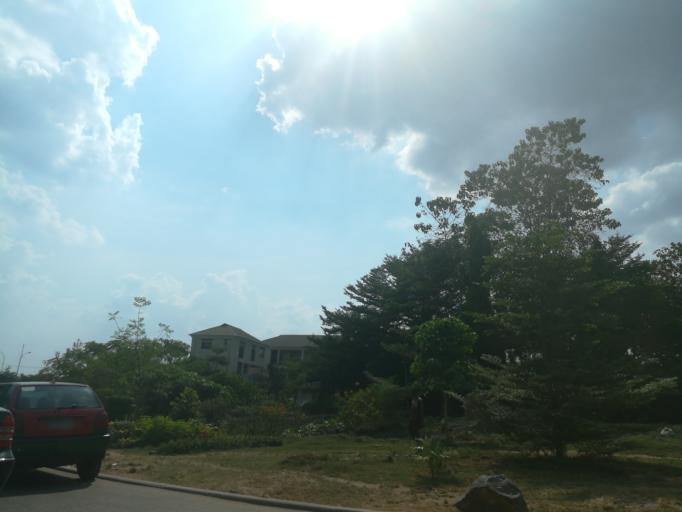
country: NG
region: Abuja Federal Capital Territory
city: Abuja
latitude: 9.0790
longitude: 7.4166
